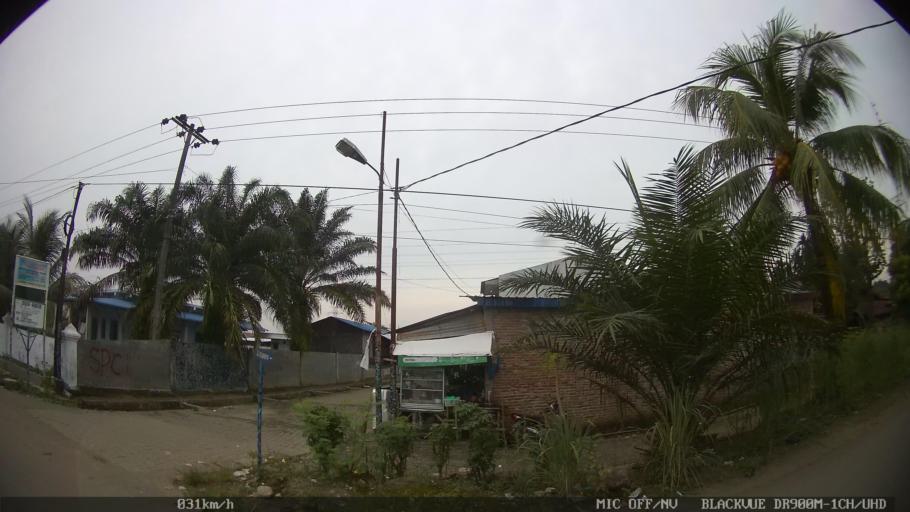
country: ID
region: North Sumatra
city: Deli Tua
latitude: 3.5515
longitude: 98.7244
